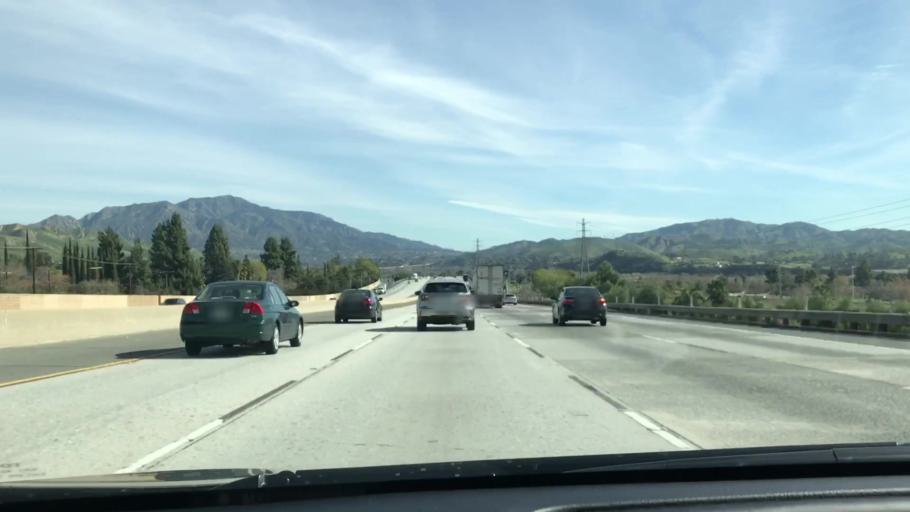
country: US
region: California
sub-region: Los Angeles County
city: San Fernando
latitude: 34.2764
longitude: -118.3877
